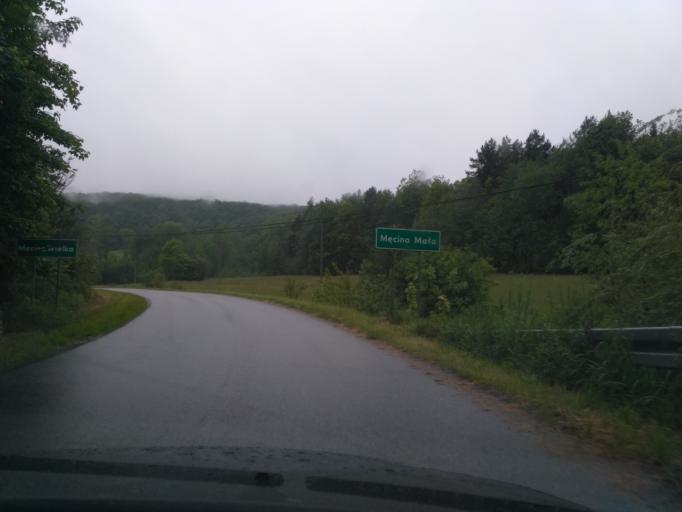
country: PL
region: Lesser Poland Voivodeship
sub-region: Powiat gorlicki
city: Kobylanka
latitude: 49.6269
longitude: 21.2542
